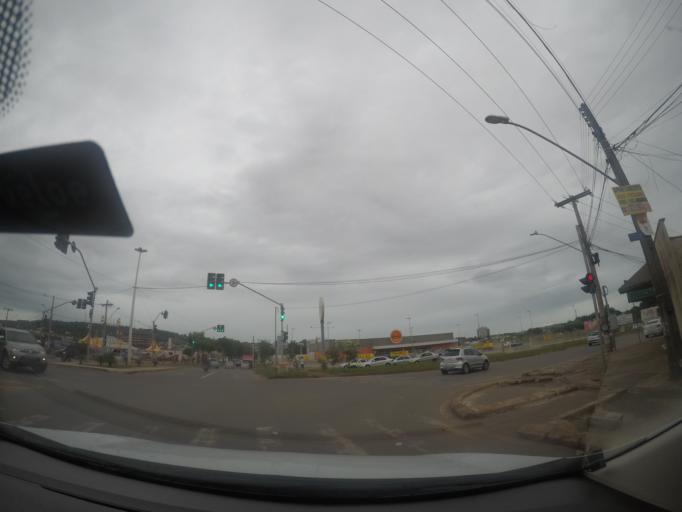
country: BR
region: Goias
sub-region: Goiania
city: Goiania
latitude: -16.6815
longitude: -49.3277
